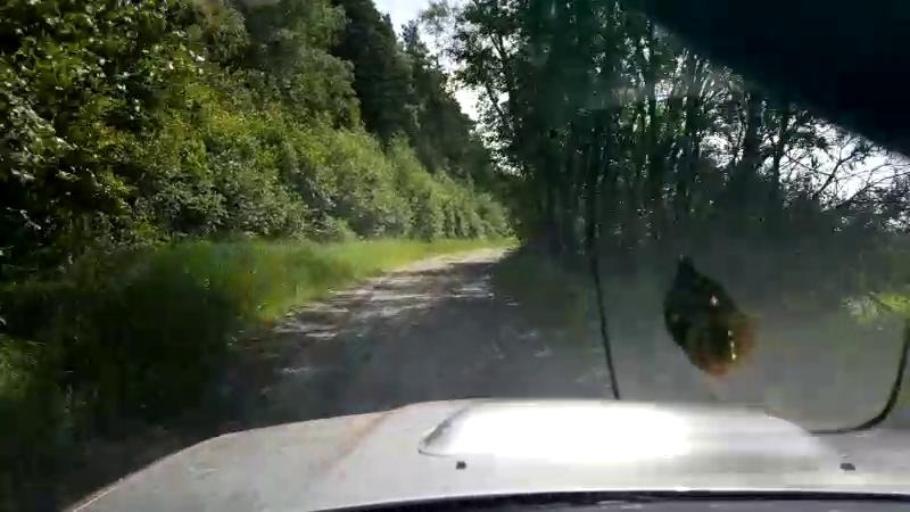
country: EE
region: Paernumaa
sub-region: Sindi linn
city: Sindi
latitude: 58.5324
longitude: 24.6650
